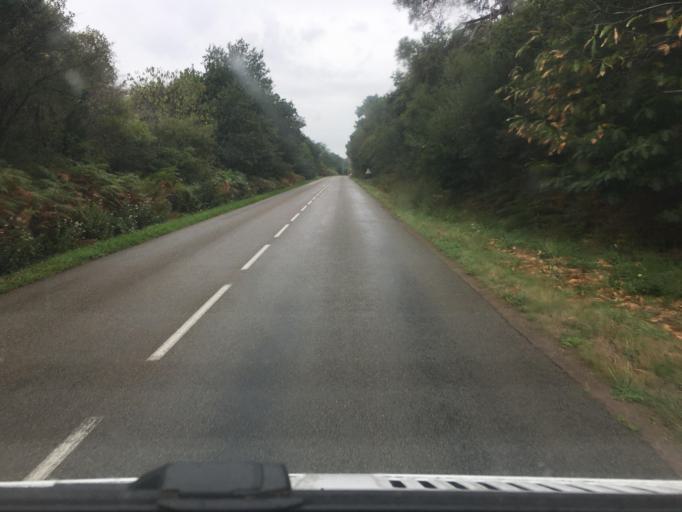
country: FR
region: Brittany
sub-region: Departement du Finistere
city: Poullan-sur-Mer
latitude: 48.0772
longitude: -4.4457
